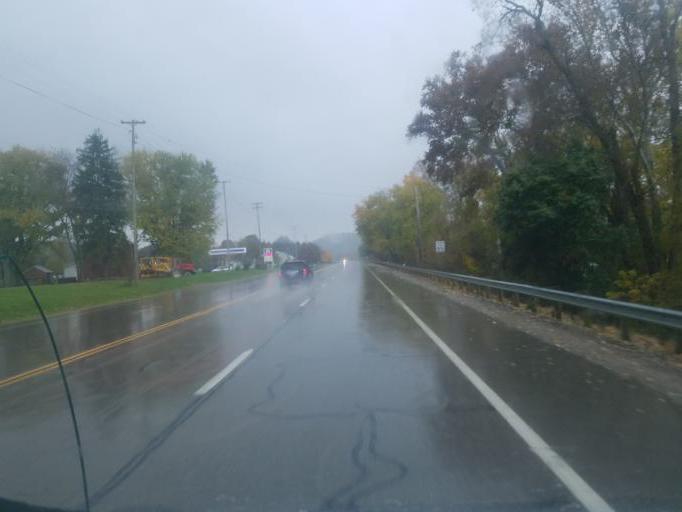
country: US
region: Ohio
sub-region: Muskingum County
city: South Zanesville
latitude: 39.9095
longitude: -82.0014
